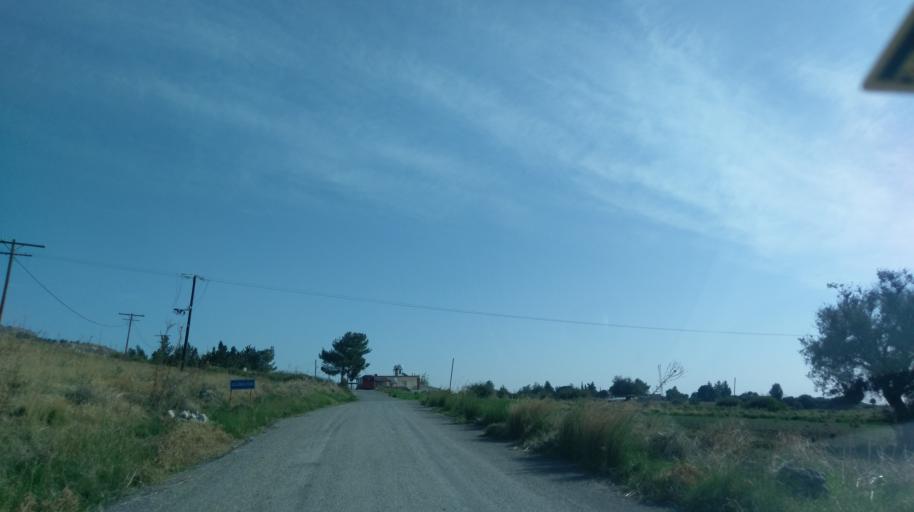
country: CY
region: Lefkosia
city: Nicosia
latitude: 35.2641
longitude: 33.4157
